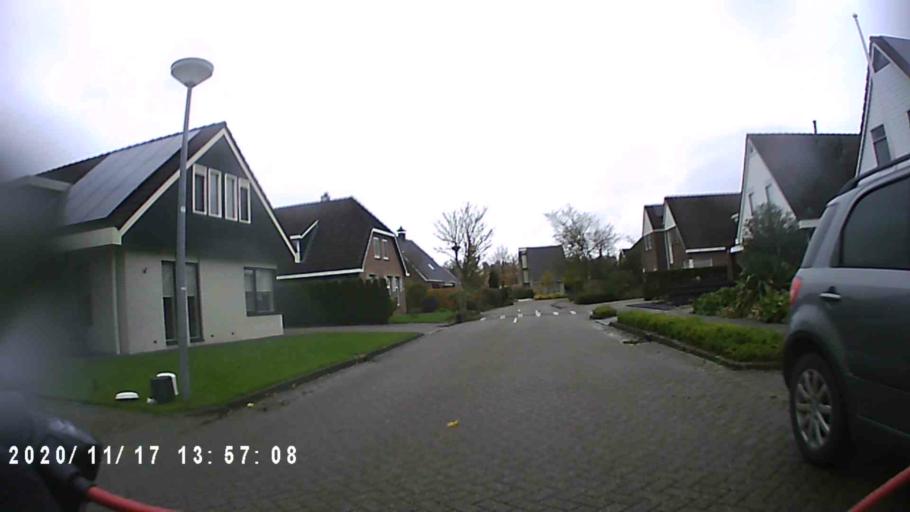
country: NL
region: Groningen
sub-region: Gemeente Zuidhorn
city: Grijpskerk
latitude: 53.2225
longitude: 6.3482
